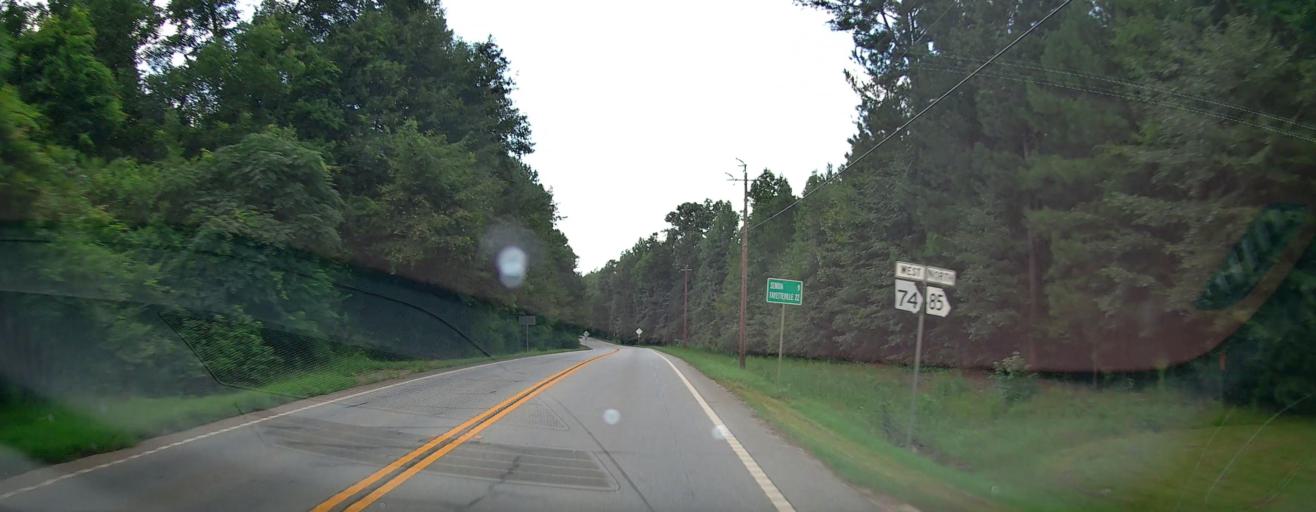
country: US
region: Georgia
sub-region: Coweta County
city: Senoia
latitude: 33.1714
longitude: -84.5805
